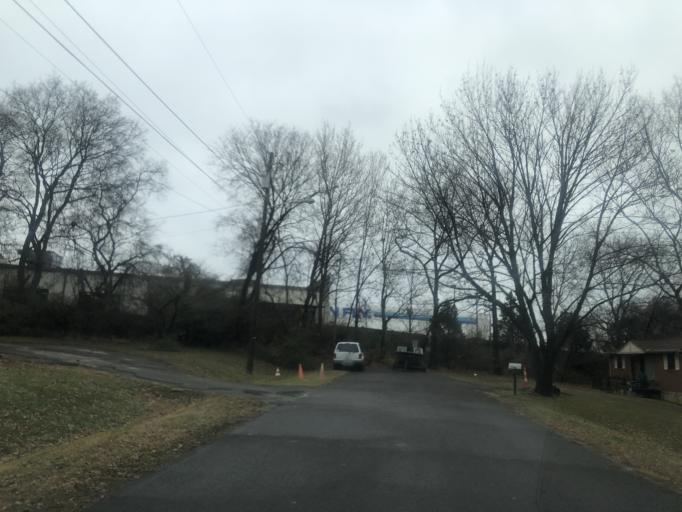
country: US
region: Tennessee
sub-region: Davidson County
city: Lakewood
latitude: 36.1454
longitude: -86.6717
